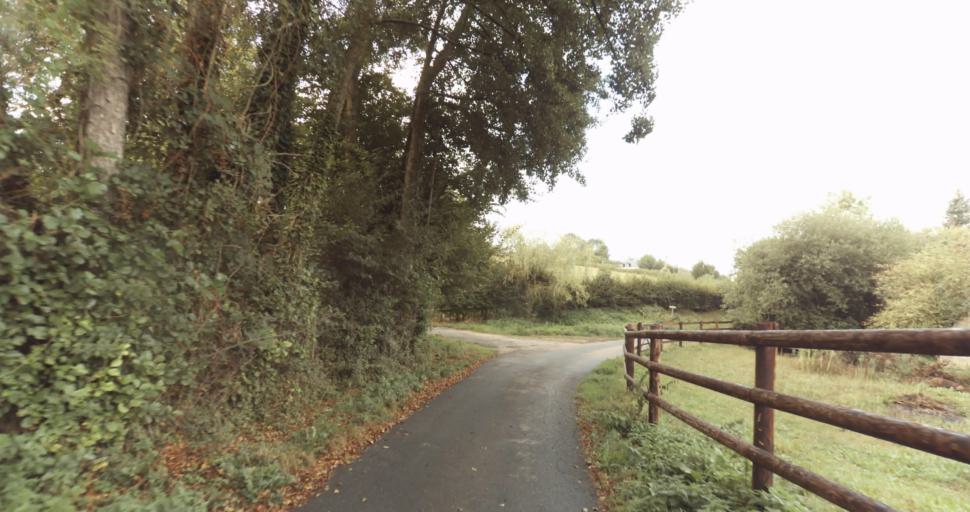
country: FR
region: Lower Normandy
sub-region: Departement de l'Orne
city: Vimoutiers
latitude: 48.9162
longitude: 0.2222
